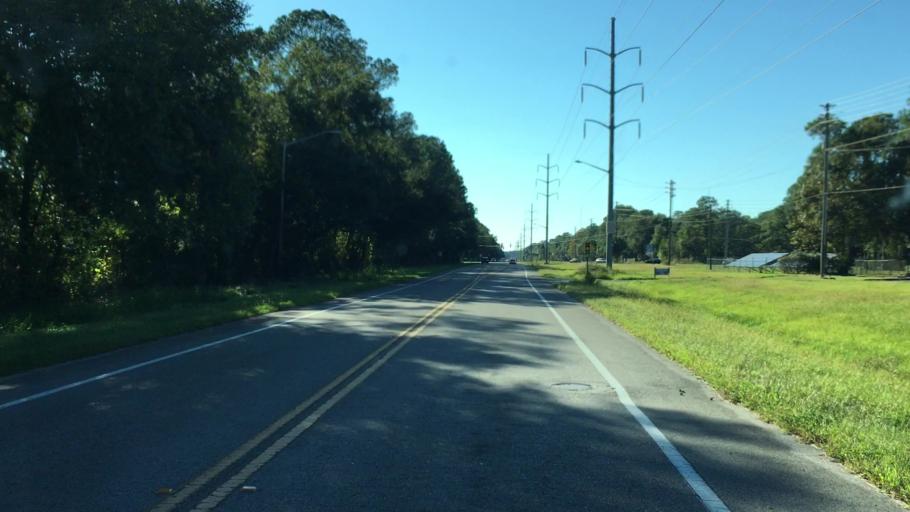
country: US
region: Florida
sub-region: Alachua County
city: Gainesville
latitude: 29.7033
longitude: -82.3606
